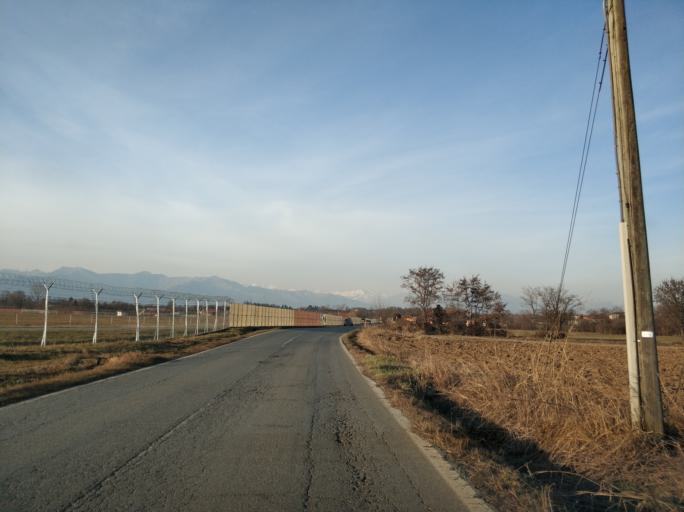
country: IT
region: Piedmont
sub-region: Provincia di Torino
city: San Francesco al Campo
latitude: 45.2163
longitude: 7.6529
